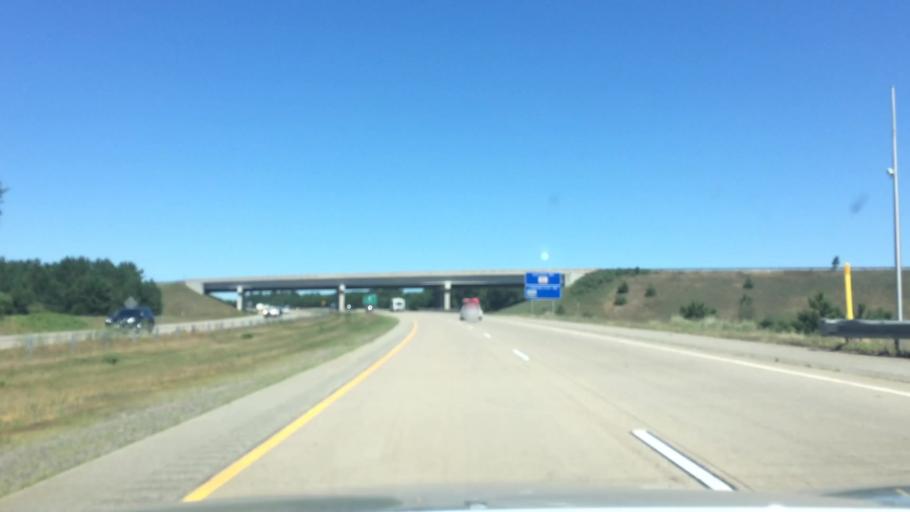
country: US
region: Wisconsin
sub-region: Marathon County
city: Rothschild
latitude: 44.8949
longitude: -89.6399
